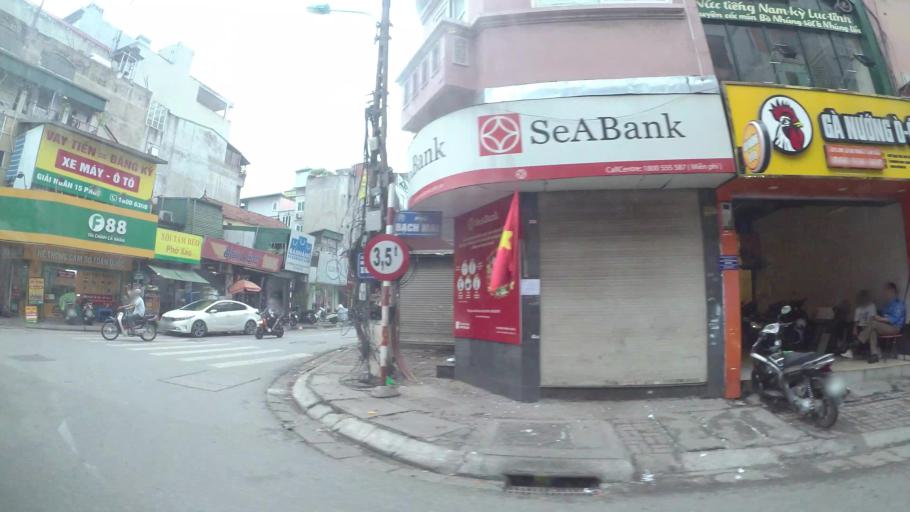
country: VN
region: Ha Noi
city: Hai BaTrung
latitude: 21.0007
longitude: 105.8506
